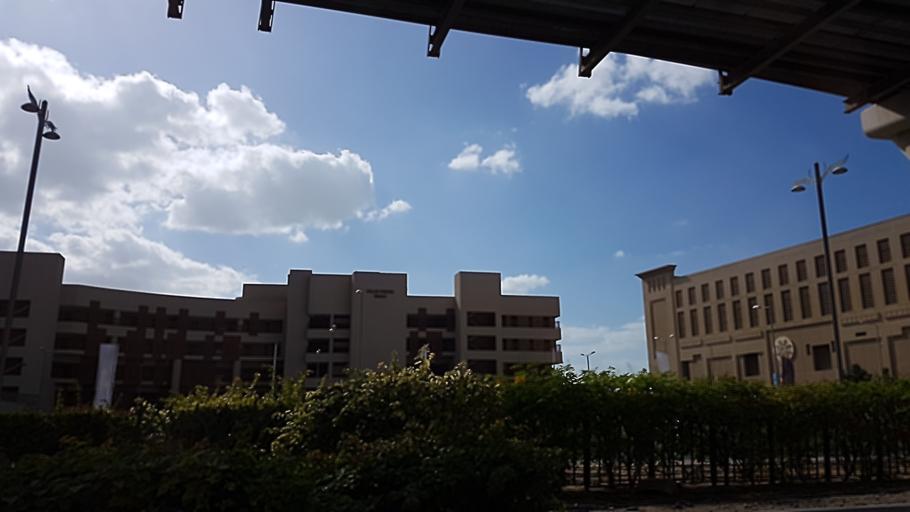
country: AE
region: Dubai
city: Dubai
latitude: 25.1161
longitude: 55.1360
